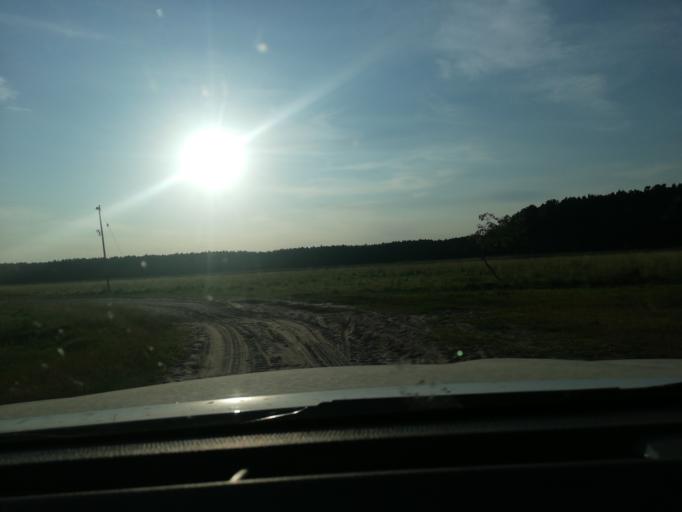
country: AR
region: Corrientes
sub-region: Departamento de San Miguel
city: San Miguel
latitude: -27.9976
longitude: -57.5264
